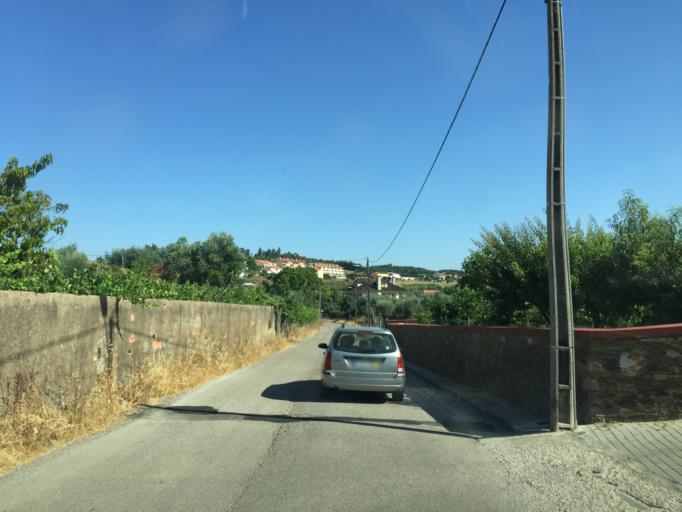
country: PT
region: Santarem
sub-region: Tomar
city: Tomar
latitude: 39.6063
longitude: -8.3309
